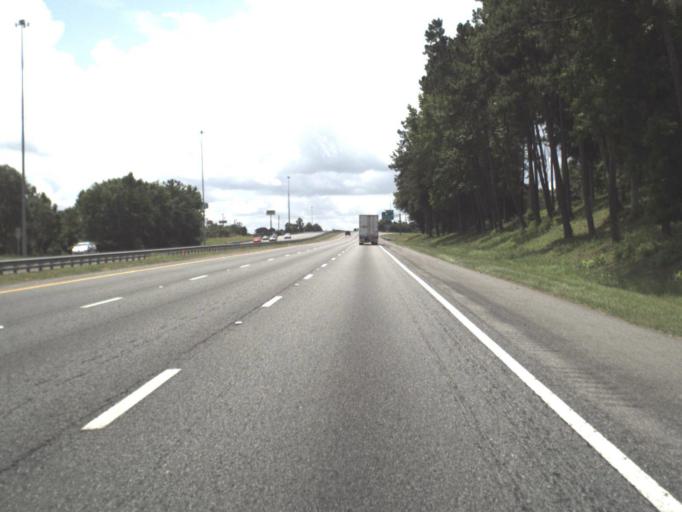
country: US
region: Florida
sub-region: Columbia County
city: Lake City
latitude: 30.1858
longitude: -82.6918
